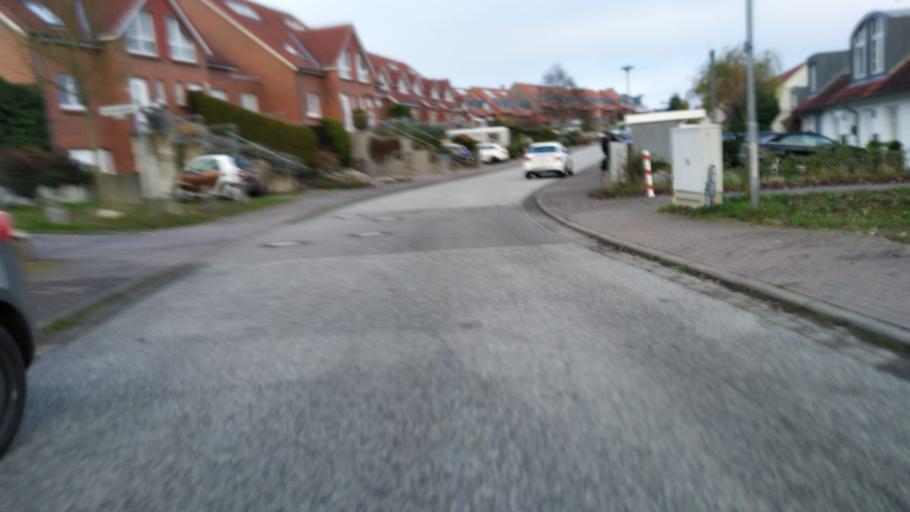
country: DE
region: Schleswig-Holstein
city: Travemuende
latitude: 53.9672
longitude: 10.8588
